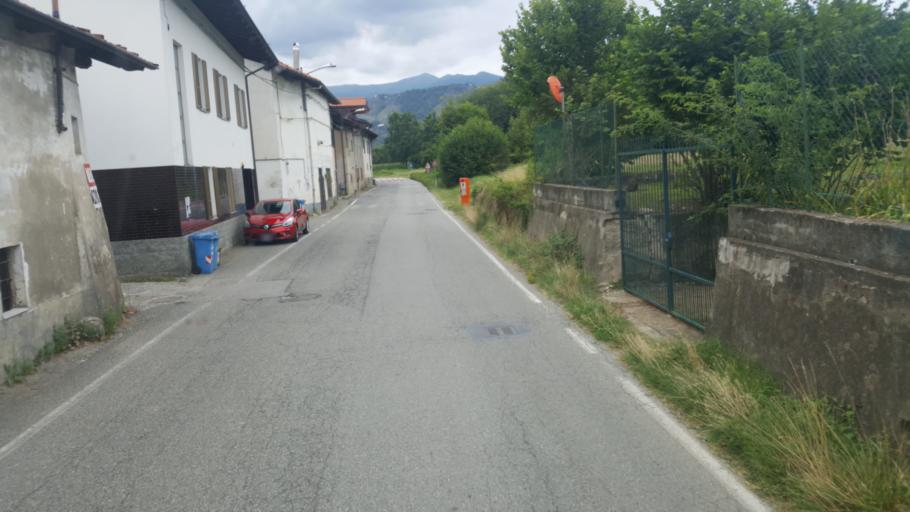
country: IT
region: Piedmont
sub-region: Provincia di Torino
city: San Ponso
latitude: 45.3514
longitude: 7.6671
